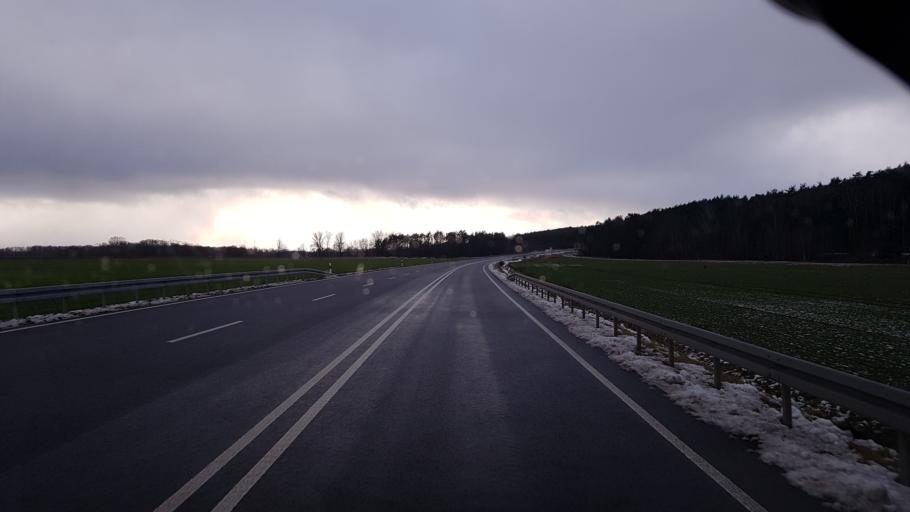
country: DE
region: Brandenburg
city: Schenkendobern
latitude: 51.8621
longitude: 14.6136
